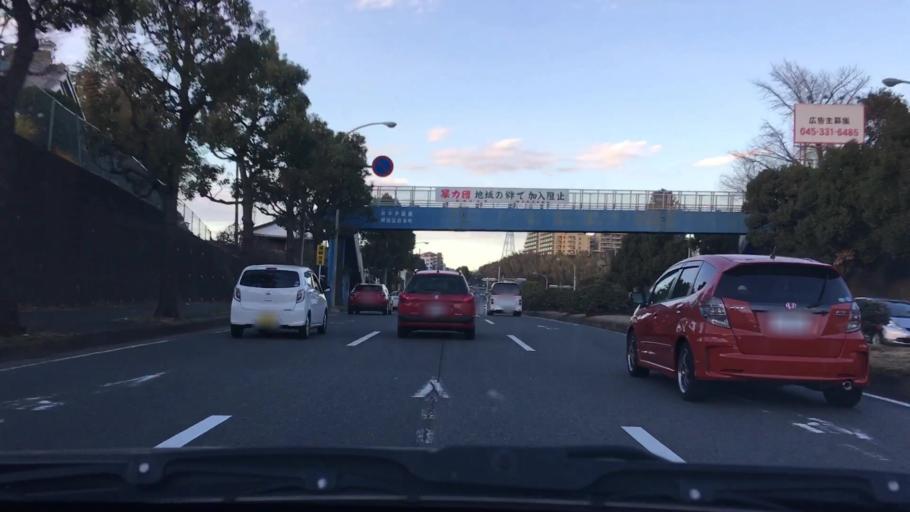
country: JP
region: Kanagawa
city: Yokohama
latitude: 35.5265
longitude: 139.5923
